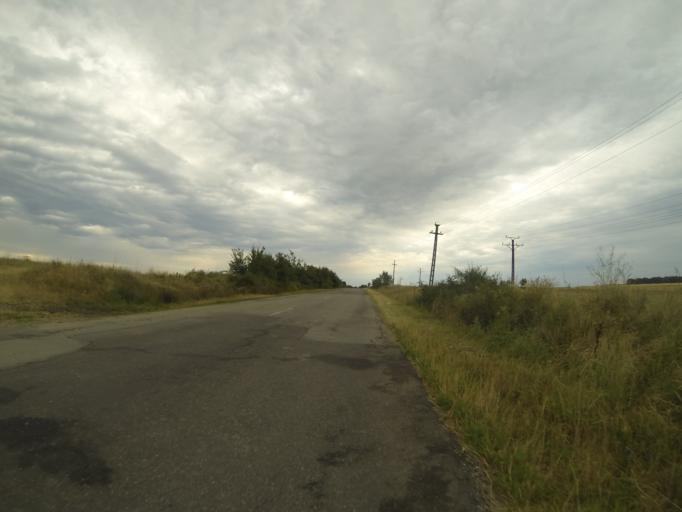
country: RO
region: Dolj
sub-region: Comuna Filiasi
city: Fratostita
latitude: 44.5851
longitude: 23.5949
